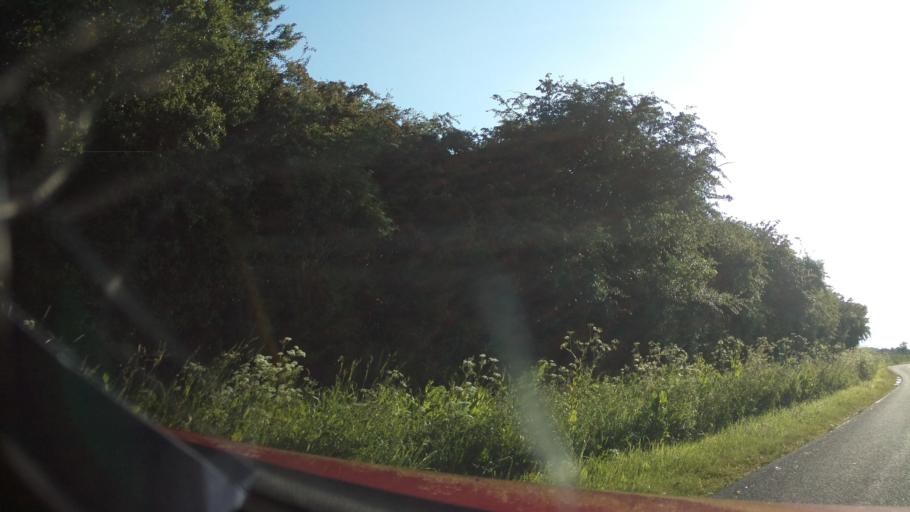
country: GB
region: England
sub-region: Lincolnshire
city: Navenby
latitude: 53.1136
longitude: -0.6043
